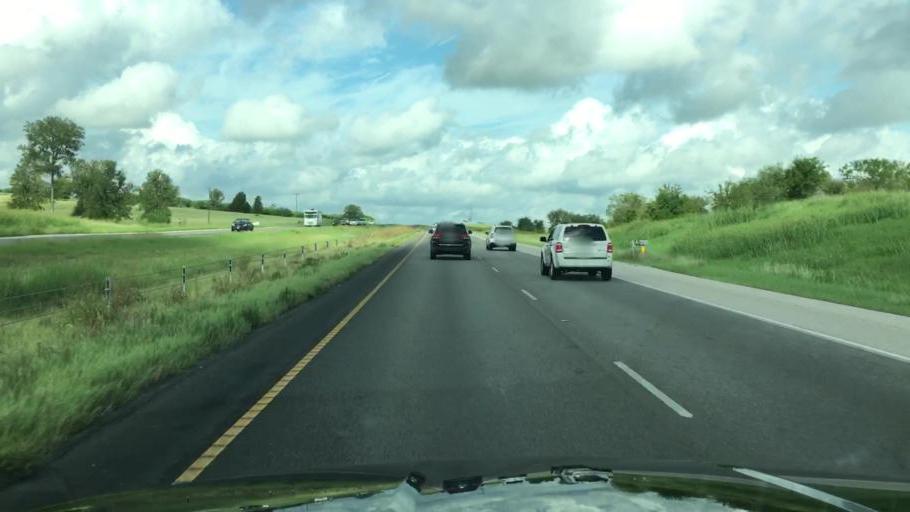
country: US
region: Texas
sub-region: Travis County
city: Garfield
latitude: 30.1697
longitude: -97.5164
